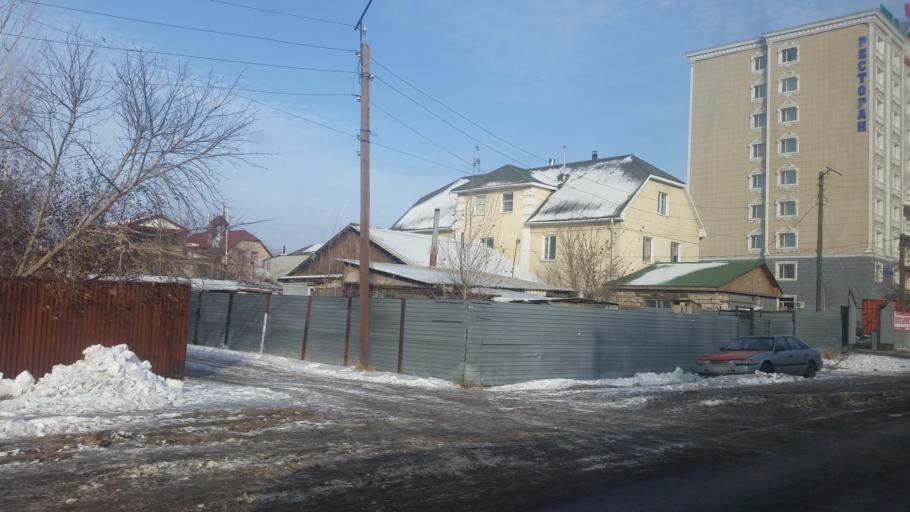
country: KZ
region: Astana Qalasy
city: Astana
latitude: 51.1883
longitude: 71.4001
